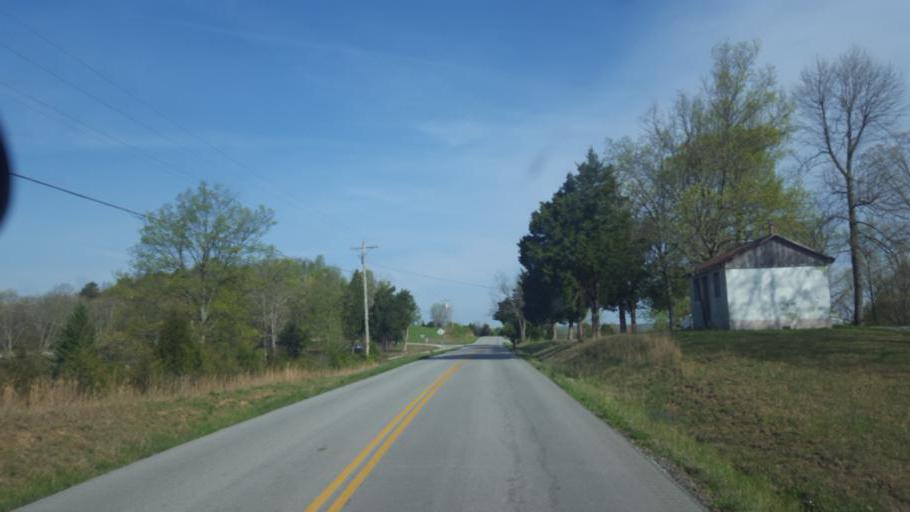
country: US
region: Kentucky
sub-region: Edmonson County
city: Brownsville
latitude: 37.3165
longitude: -86.1078
